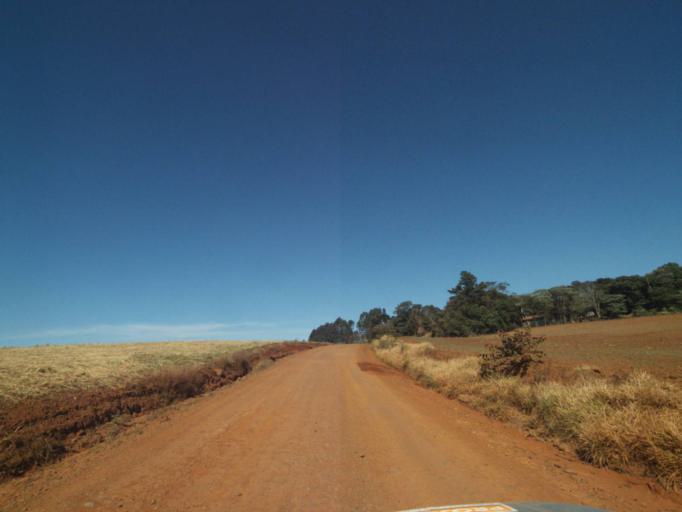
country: BR
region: Parana
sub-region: Tibagi
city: Tibagi
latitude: -24.5830
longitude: -50.6108
